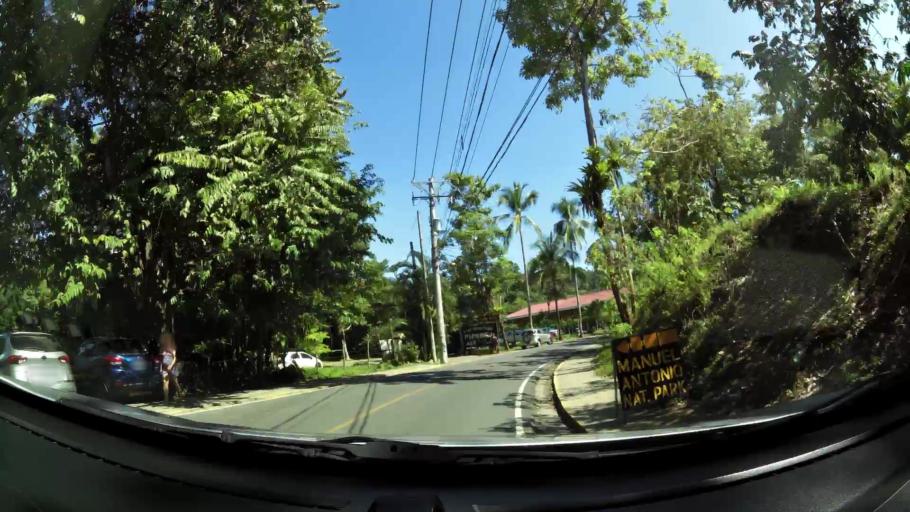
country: CR
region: Puntarenas
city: Quepos
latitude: 9.3906
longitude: -84.1482
